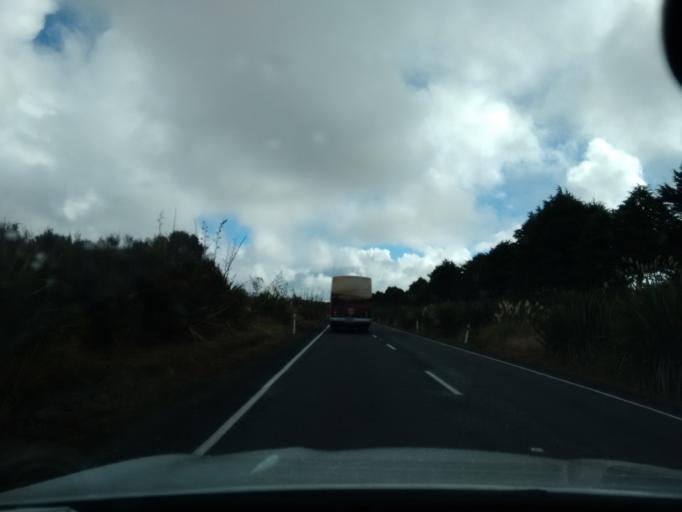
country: NZ
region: Manawatu-Wanganui
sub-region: Ruapehu District
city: Waiouru
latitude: -39.1808
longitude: 175.4467
